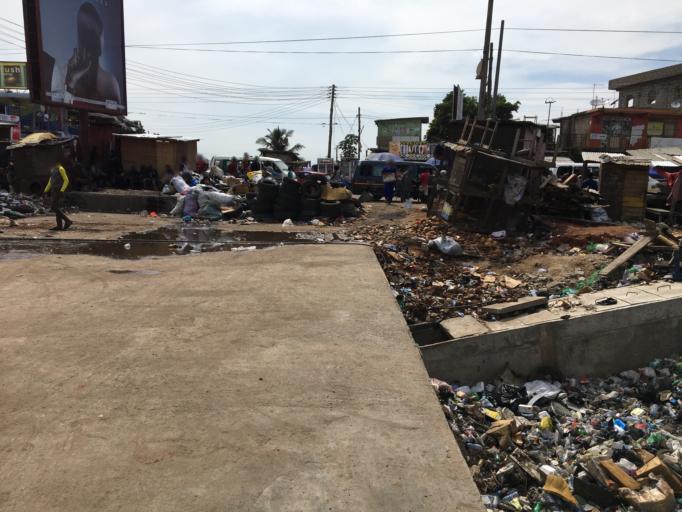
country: GH
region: Greater Accra
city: Accra
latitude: 5.5884
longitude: -0.1963
